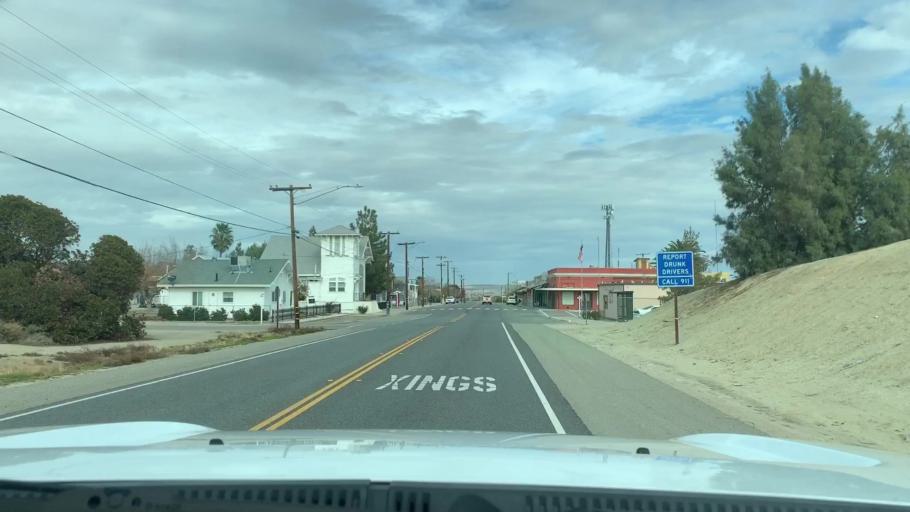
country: US
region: California
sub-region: Kern County
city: Maricopa
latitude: 35.0618
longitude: -119.4017
